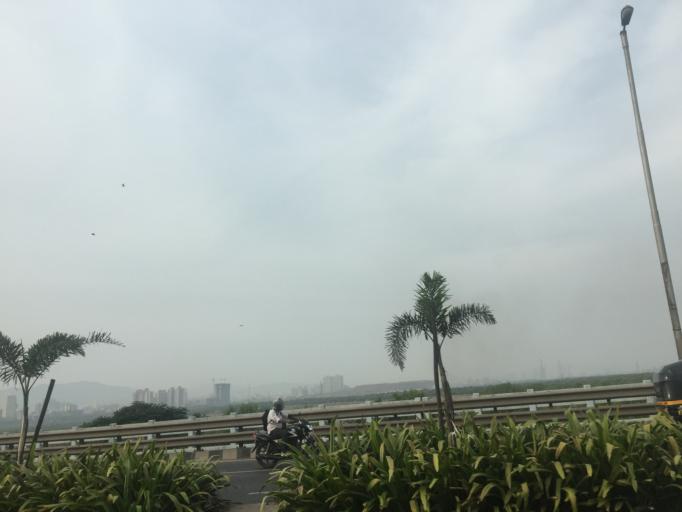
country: IN
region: Maharashtra
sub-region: Thane
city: Airoli
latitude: 19.1516
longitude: 72.9755
